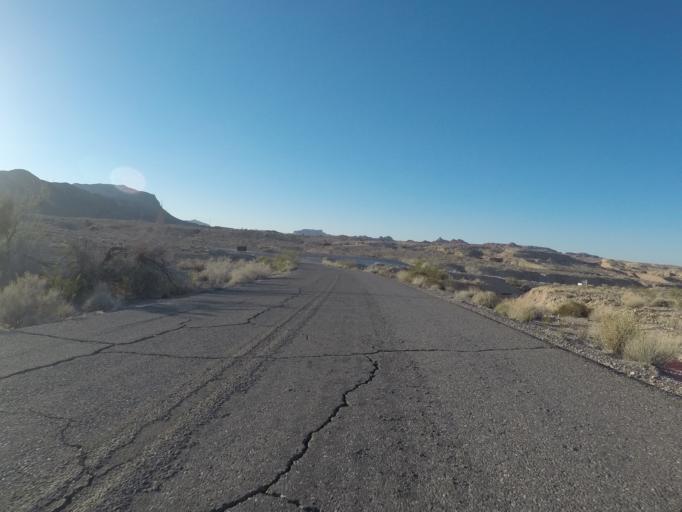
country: US
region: Nevada
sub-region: Clark County
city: Moapa Valley
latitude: 36.3942
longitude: -114.4241
